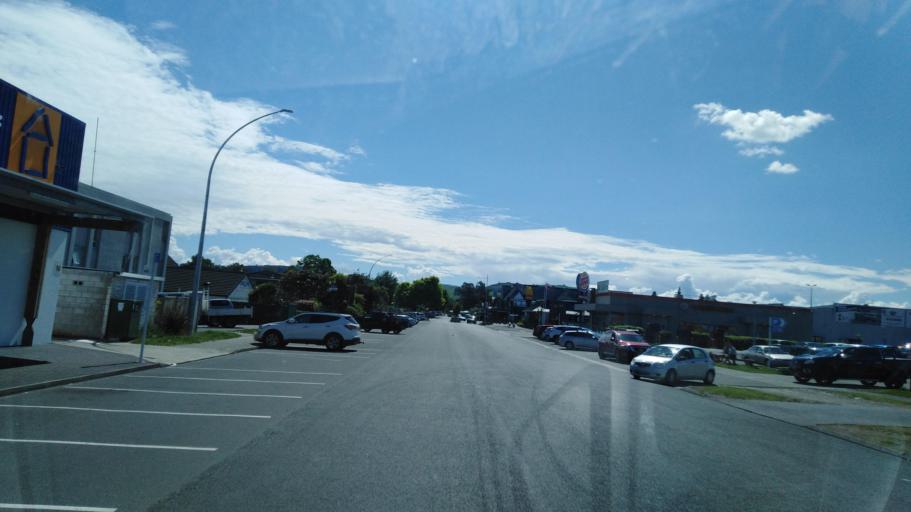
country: NZ
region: Waikato
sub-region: Taupo District
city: Taupo
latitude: -38.6905
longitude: 176.0731
